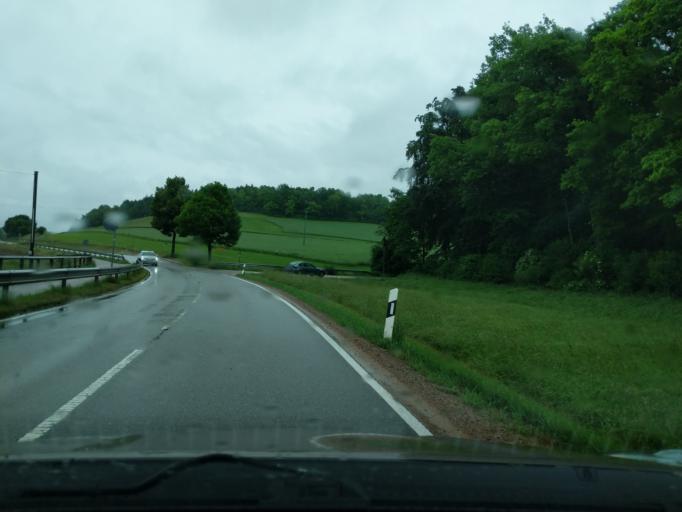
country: DE
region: Bavaria
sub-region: Upper Palatinate
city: Pettendorf
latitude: 49.0424
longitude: 12.0245
